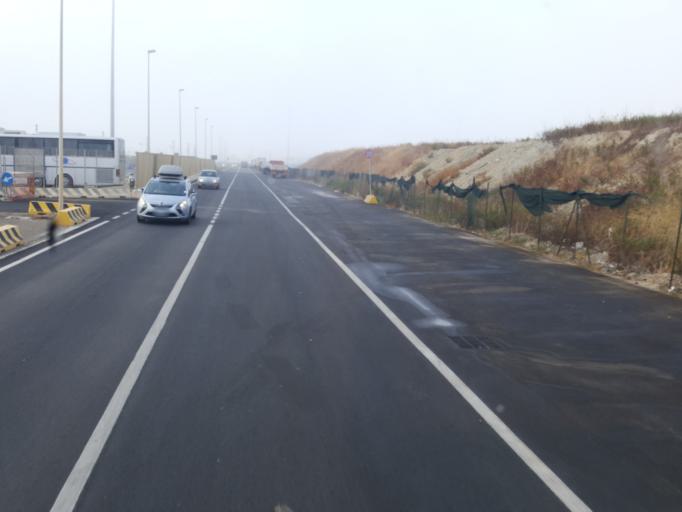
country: IT
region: Latium
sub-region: Citta metropolitana di Roma Capitale
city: Aurelia
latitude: 42.1135
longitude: 11.7703
